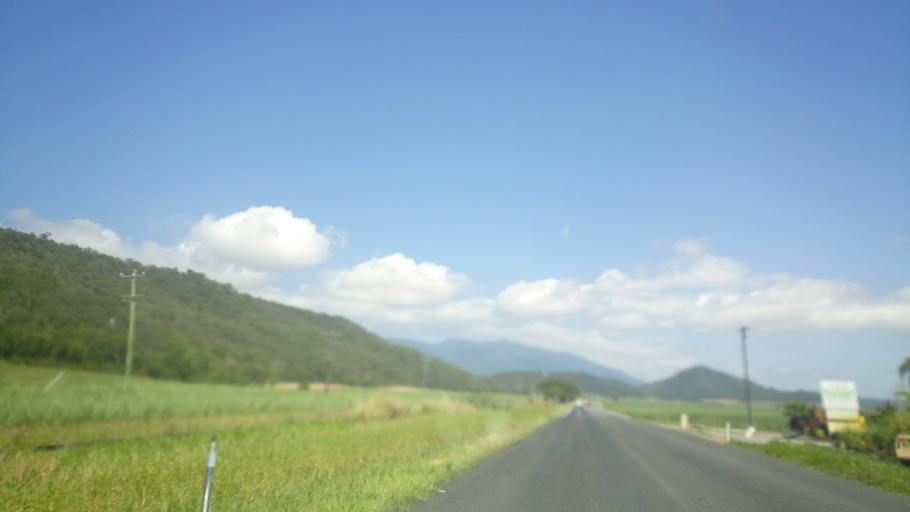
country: AU
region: Queensland
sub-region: Cairns
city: Port Douglas
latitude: -16.4887
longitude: 145.4182
